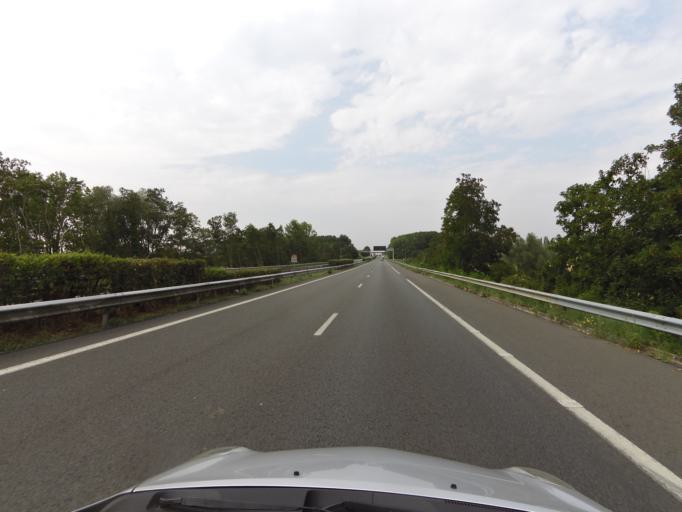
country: FR
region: Nord-Pas-de-Calais
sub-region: Departement du Nord
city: Marcoing
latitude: 50.1153
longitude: 3.1587
